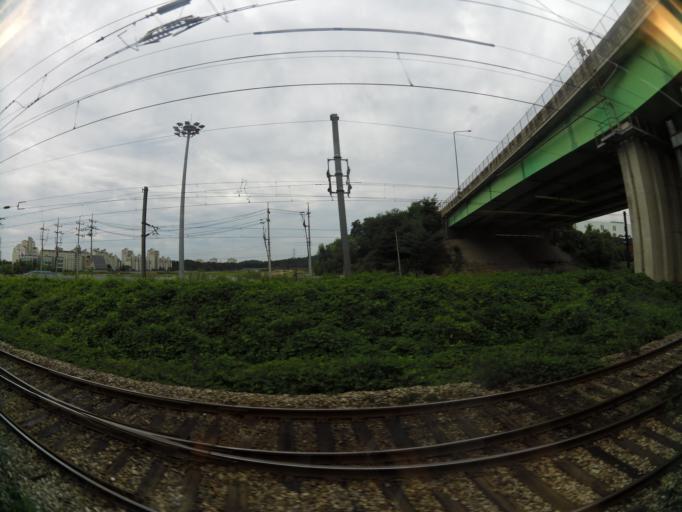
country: KR
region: Gyeonggi-do
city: Anyang-si
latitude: 37.3277
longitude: 126.9479
